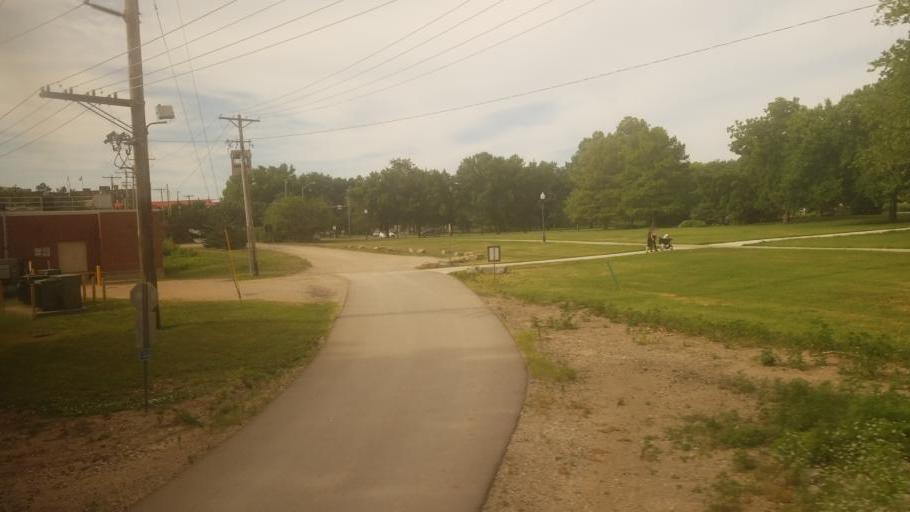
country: US
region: Kansas
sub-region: Douglas County
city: Lawrence
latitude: 38.9745
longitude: -95.2387
